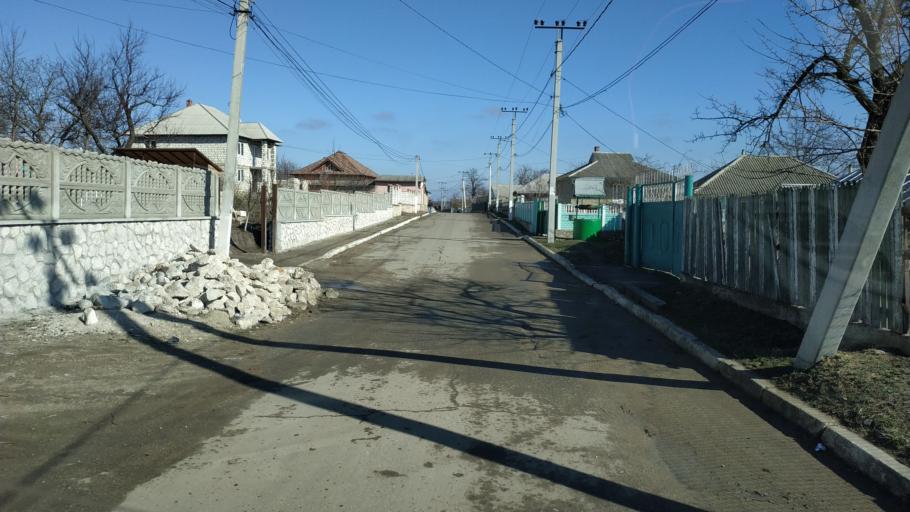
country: MD
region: Hincesti
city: Hincesti
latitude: 46.9205
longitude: 28.6260
